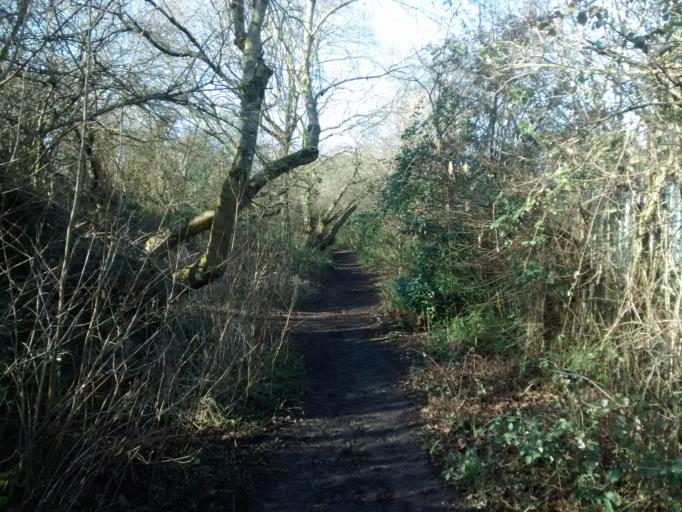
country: GB
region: England
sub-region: South Gloucestershire
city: Almondsbury
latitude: 51.5404
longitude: -2.5827
